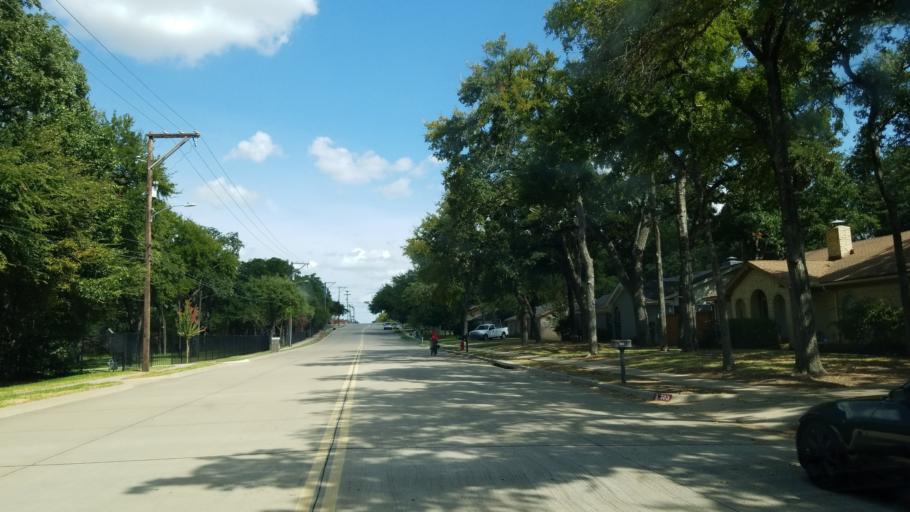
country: US
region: Texas
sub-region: Tarrant County
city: Euless
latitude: 32.8591
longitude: -97.0850
